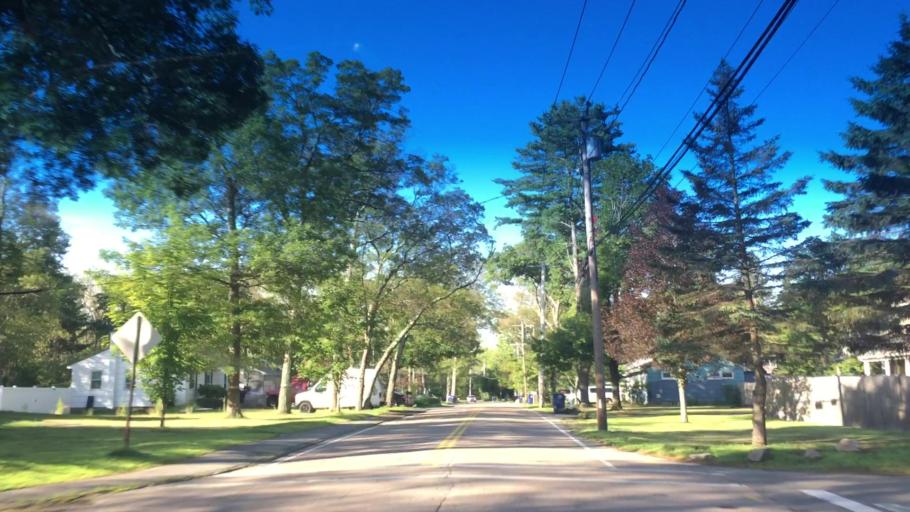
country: US
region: Massachusetts
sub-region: Norfolk County
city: Medway
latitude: 42.1548
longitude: -71.3908
